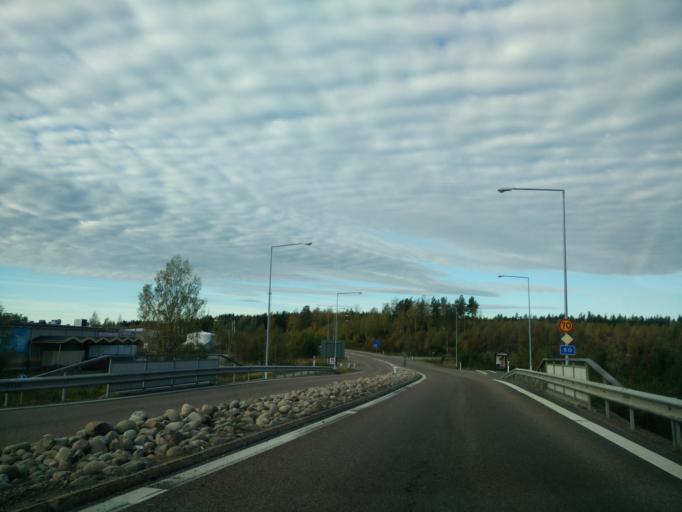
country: SE
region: Gaevleborg
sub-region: Soderhamns Kommun
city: Soderhamn
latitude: 61.2972
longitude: 17.0217
